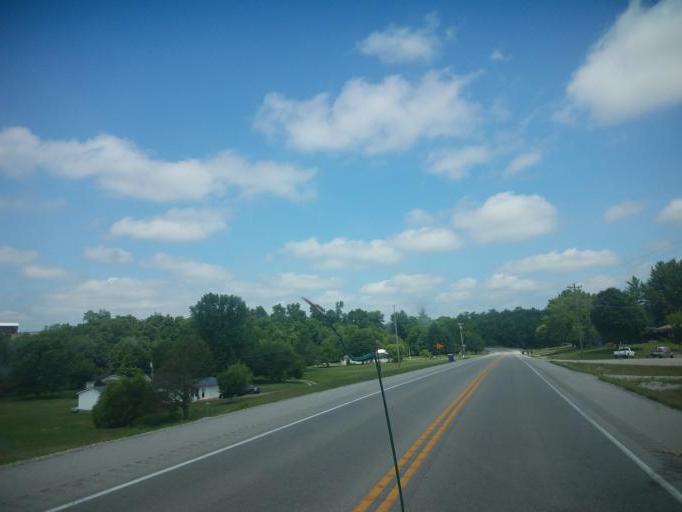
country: US
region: Kentucky
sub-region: Barren County
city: Glasgow
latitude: 36.9350
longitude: -85.8229
